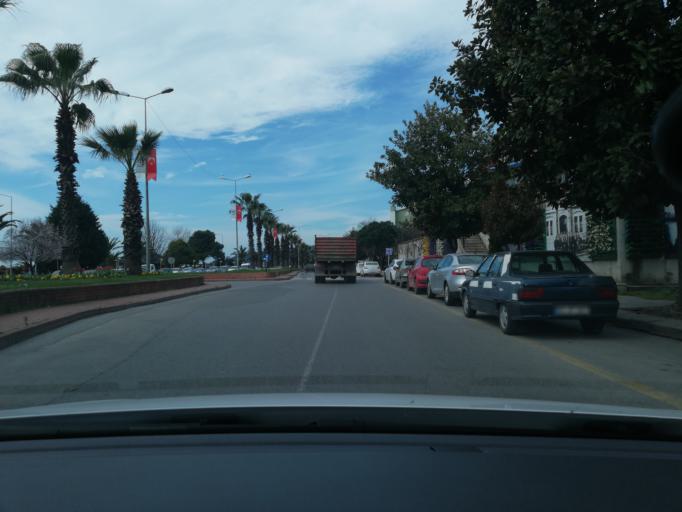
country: TR
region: Zonguldak
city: Eregli
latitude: 41.2811
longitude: 31.4177
